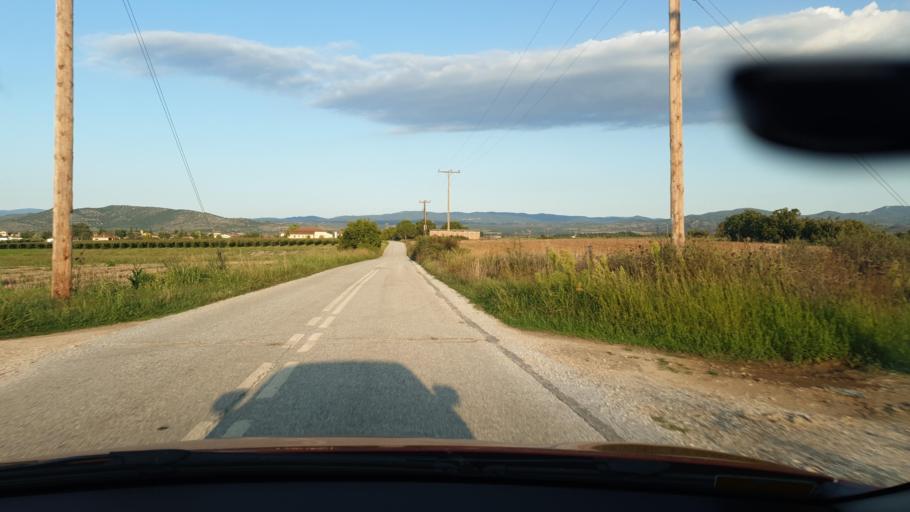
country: GR
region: Central Macedonia
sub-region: Nomos Thessalonikis
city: Nea Apollonia
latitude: 40.5558
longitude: 23.4603
